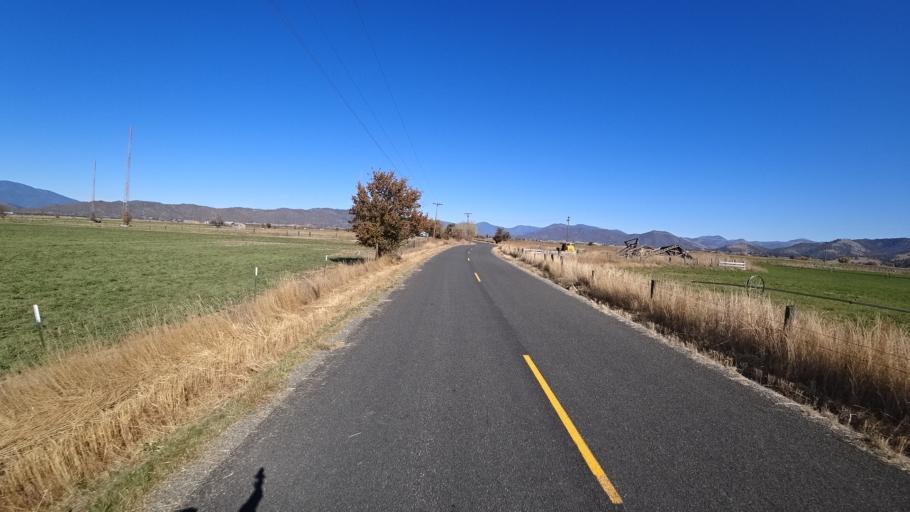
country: US
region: California
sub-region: Siskiyou County
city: Yreka
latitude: 41.5259
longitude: -122.8582
